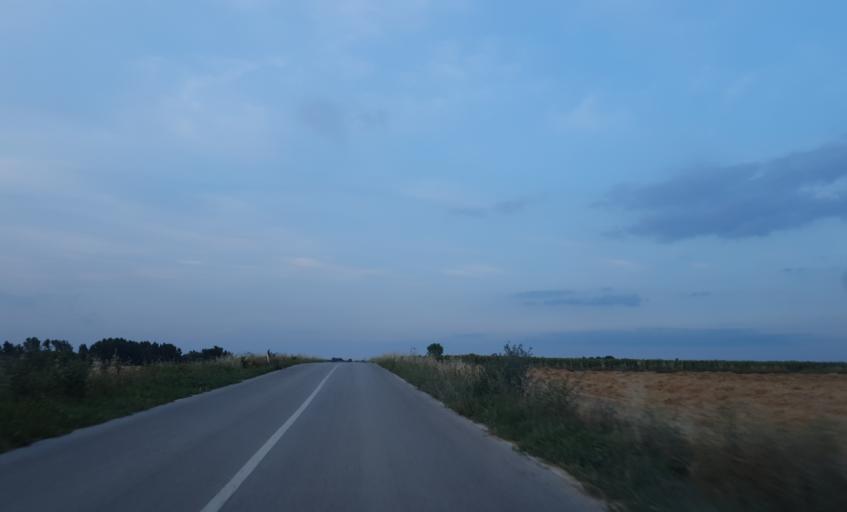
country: TR
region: Tekirdag
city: Beyazkoy
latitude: 41.4012
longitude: 27.6395
